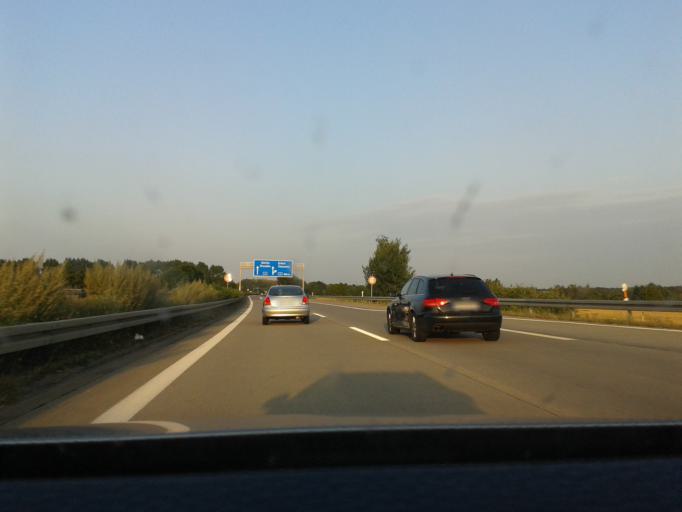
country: DE
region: Saxony
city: Nossen
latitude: 51.0556
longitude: 13.3509
